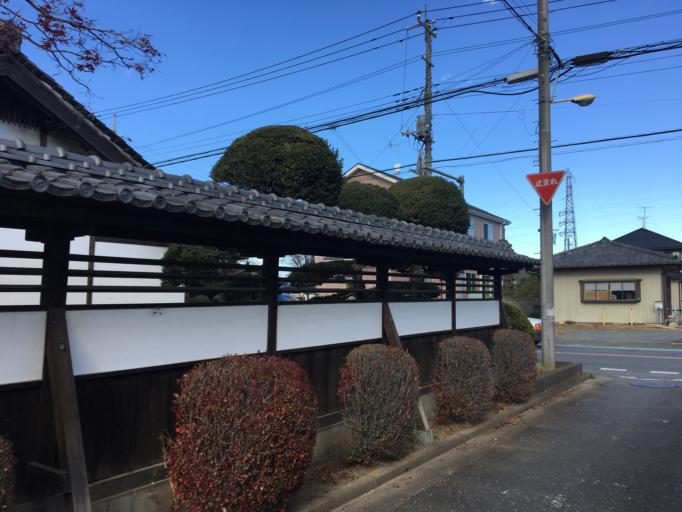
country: JP
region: Saitama
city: Ogawa
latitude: 36.0428
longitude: 139.3259
